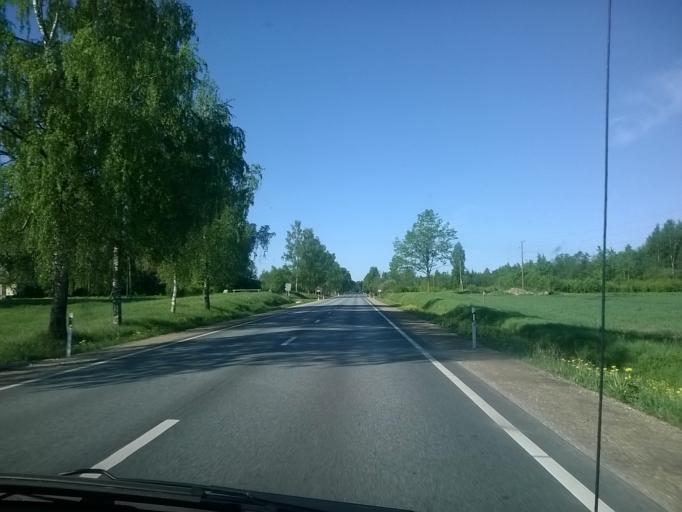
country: LV
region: Valmieras Rajons
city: Valmiera
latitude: 57.5748
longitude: 25.4803
